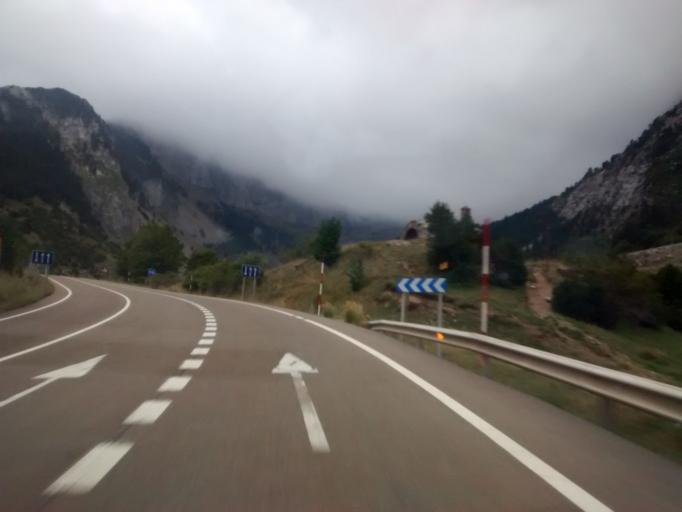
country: ES
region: Aragon
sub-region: Provincia de Huesca
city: Canfranc
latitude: 42.7748
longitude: -0.5157
